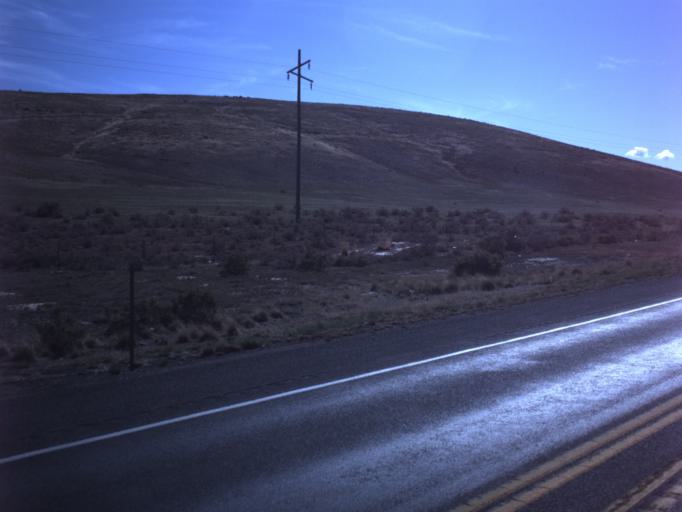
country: US
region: Utah
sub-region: Sanpete County
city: Gunnison
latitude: 39.2059
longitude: -111.8481
